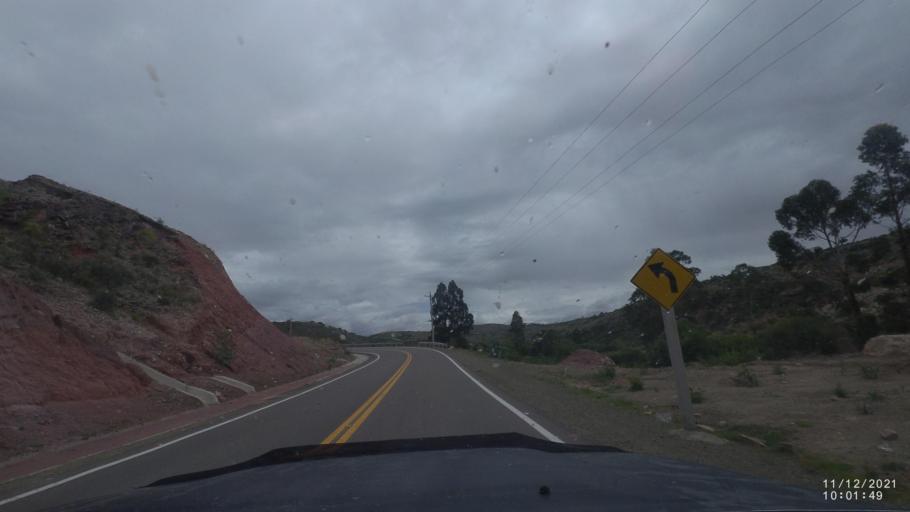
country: BO
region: Cochabamba
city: Cliza
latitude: -17.7255
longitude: -65.9311
